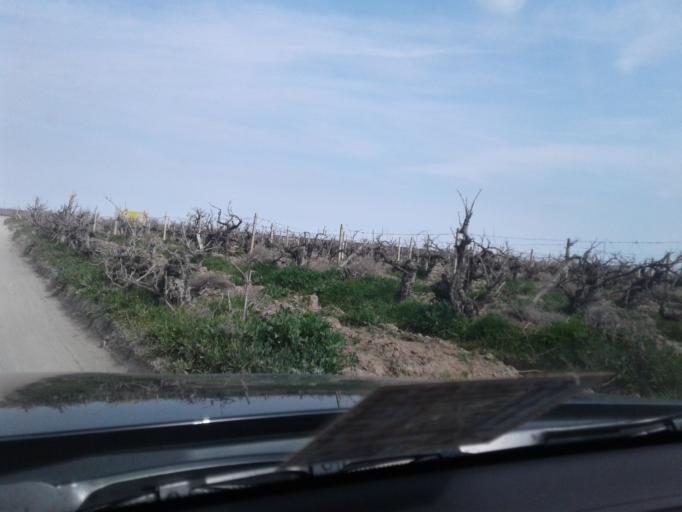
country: TM
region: Ahal
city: Abadan
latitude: 38.1180
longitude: 58.3525
